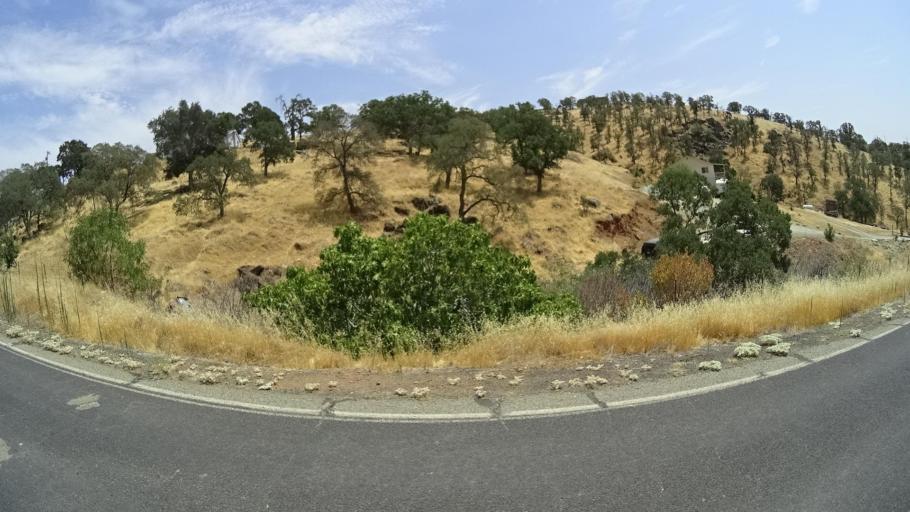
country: US
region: California
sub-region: Tuolumne County
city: Jamestown
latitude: 37.6395
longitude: -120.3442
